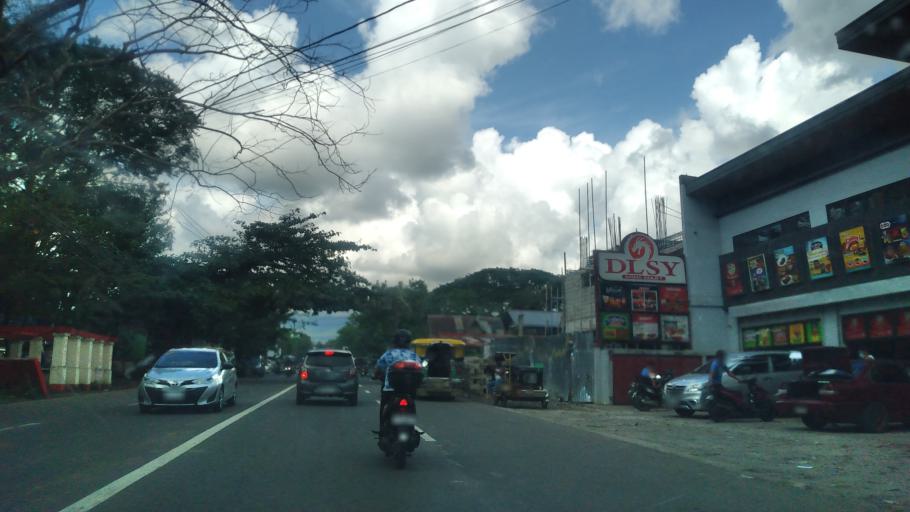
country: PH
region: Calabarzon
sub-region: Province of Quezon
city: Isabang
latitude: 13.9555
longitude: 121.5723
